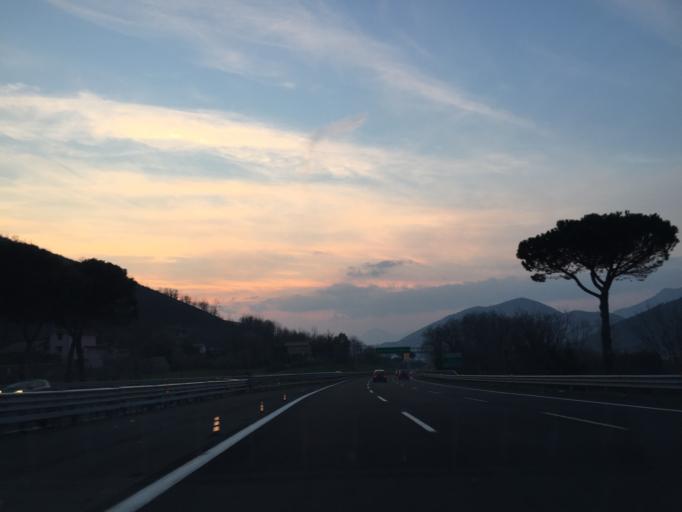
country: IT
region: Campania
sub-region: Provincia di Salerno
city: Mercato San Severino
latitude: 40.7710
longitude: 14.7393
